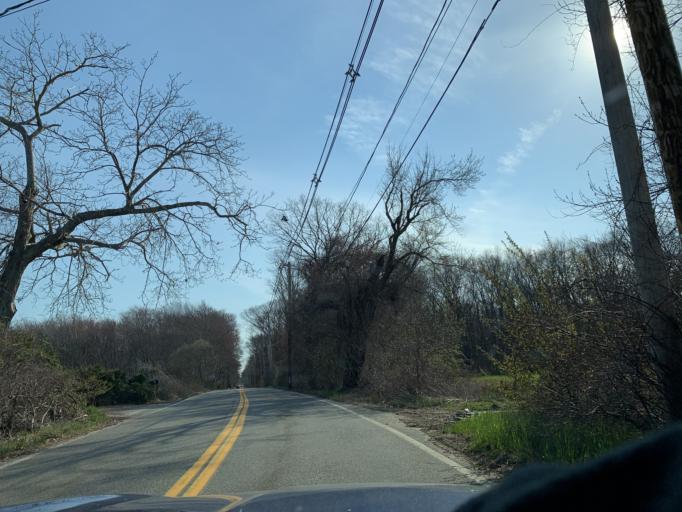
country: US
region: Rhode Island
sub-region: Kent County
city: West Warwick
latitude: 41.7483
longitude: -71.5263
